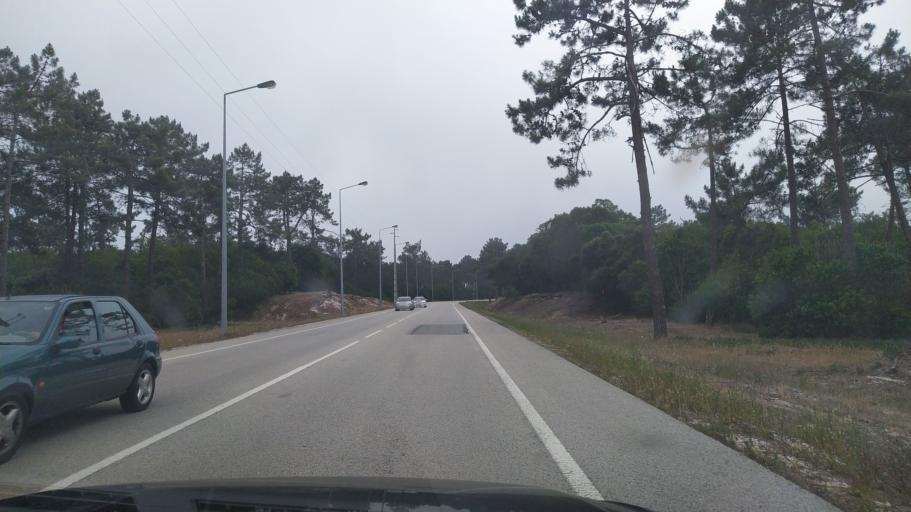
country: PT
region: Aveiro
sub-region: Ilhavo
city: Gafanha da Nazare
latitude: 40.6179
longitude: -8.7146
